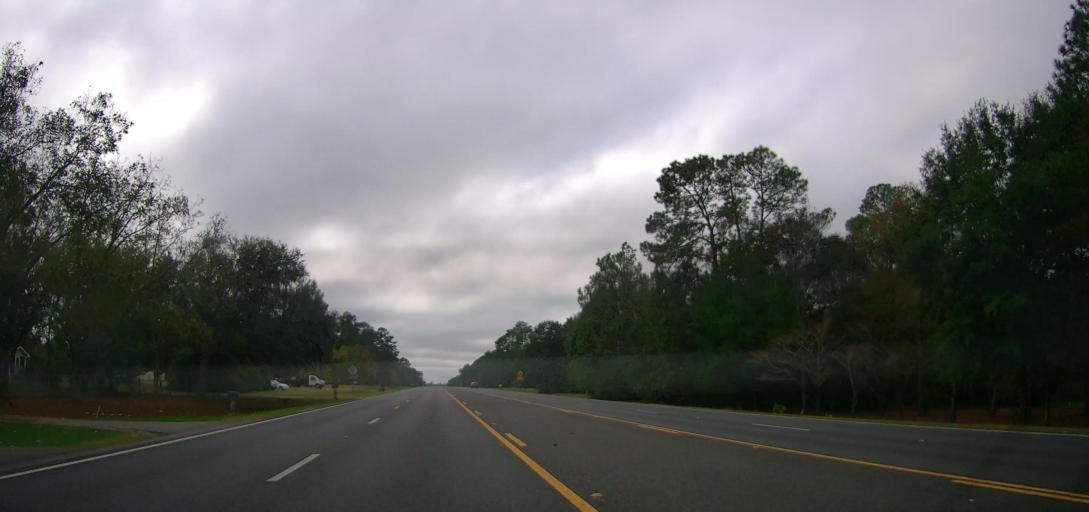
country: US
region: Georgia
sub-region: Colquitt County
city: Moultrie
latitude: 31.0928
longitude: -83.8054
